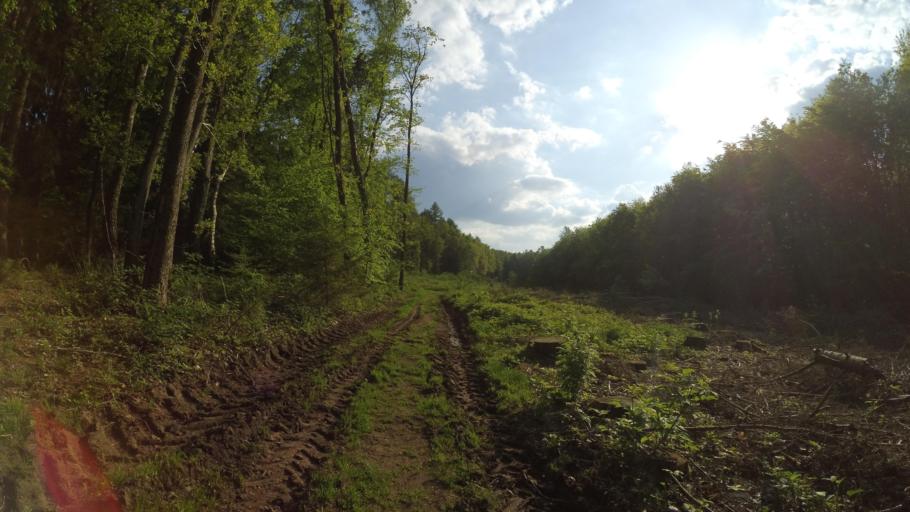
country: DE
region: Saarland
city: Hangard
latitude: 49.4140
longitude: 7.2243
